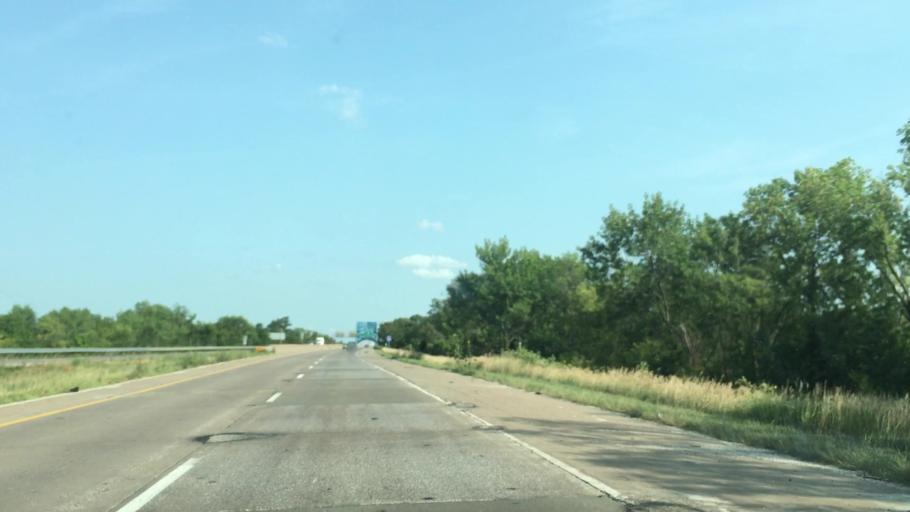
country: US
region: Illinois
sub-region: Rock Island County
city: Rock Island
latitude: 41.4872
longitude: -90.6432
